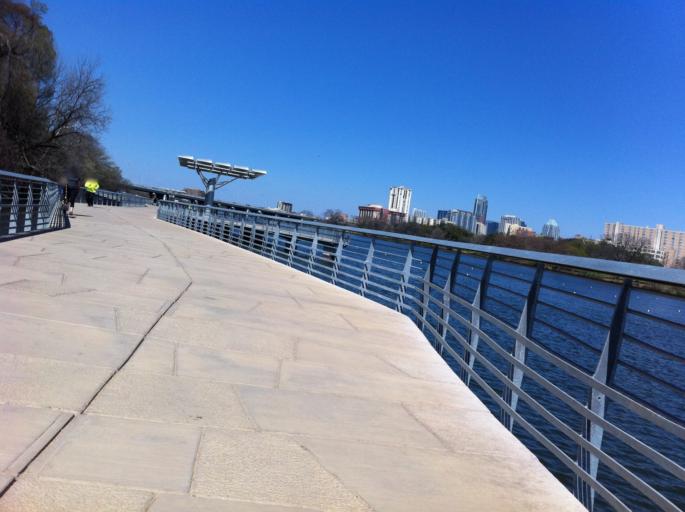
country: US
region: Texas
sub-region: Travis County
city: Austin
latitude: 30.2480
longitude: -97.7315
